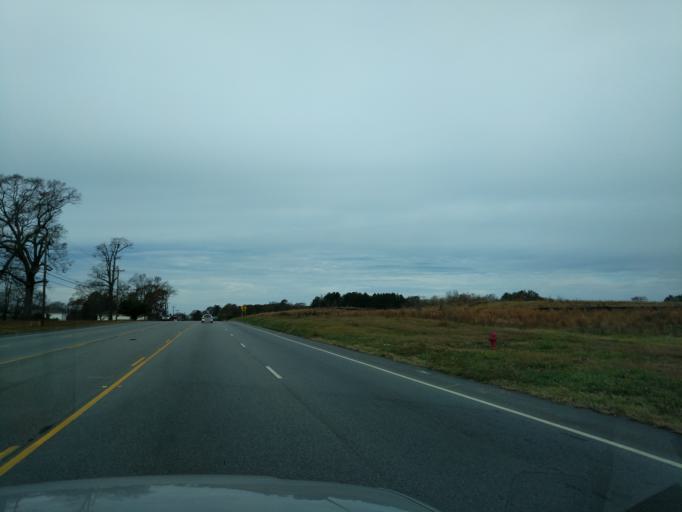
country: US
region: South Carolina
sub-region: Anderson County
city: Northlake
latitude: 34.5901
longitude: -82.7451
